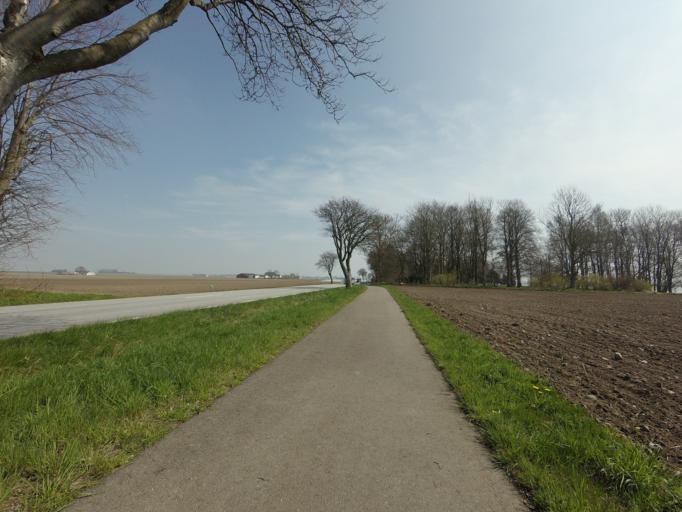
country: SE
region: Skane
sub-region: Skurups Kommun
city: Skivarp
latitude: 55.3861
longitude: 13.5659
